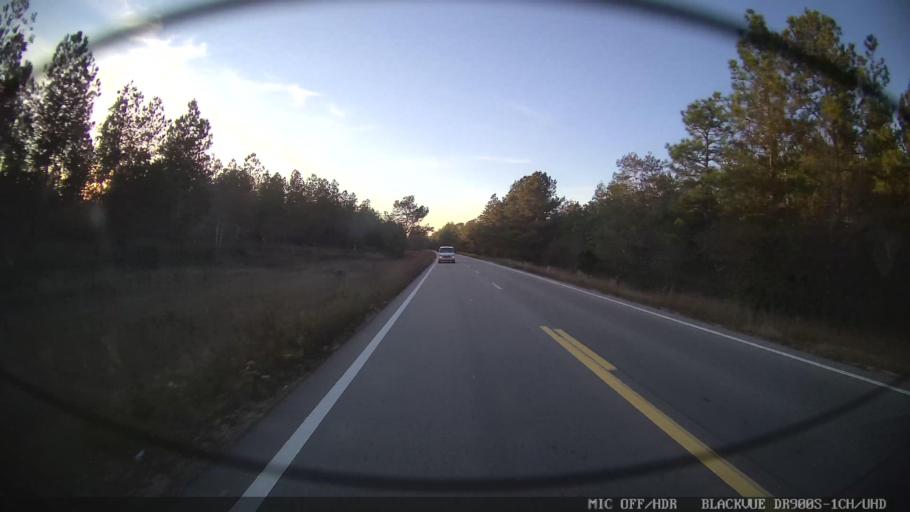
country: US
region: Mississippi
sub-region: Lamar County
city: Lumberton
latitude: 31.0004
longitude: -89.3064
